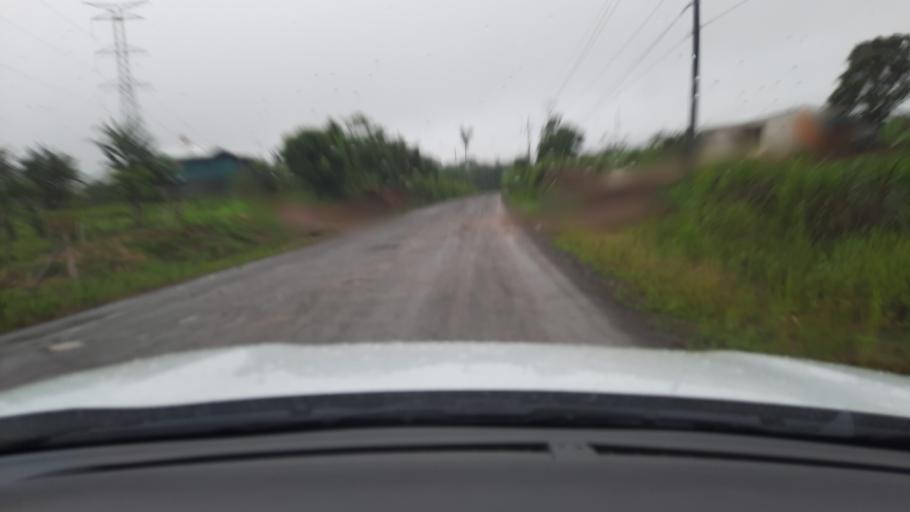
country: NI
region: Rivas
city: Cardenas
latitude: 11.0343
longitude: -85.3694
